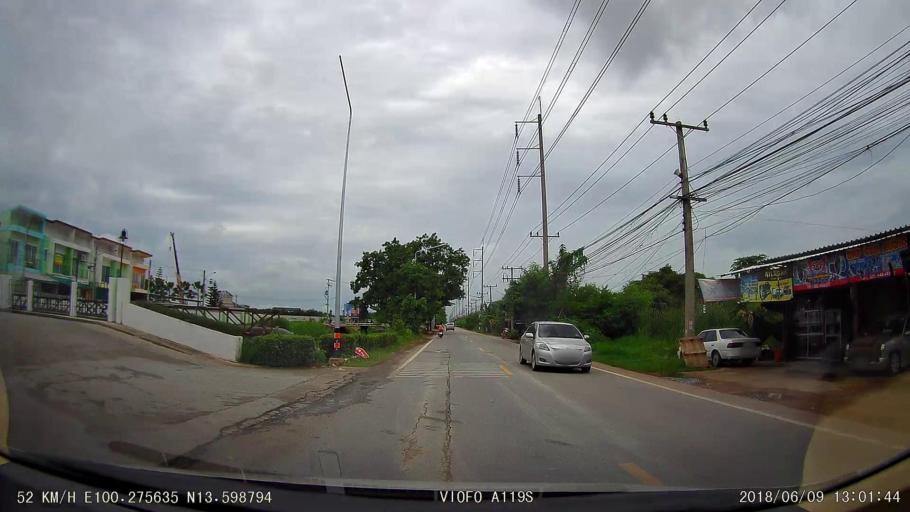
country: TH
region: Samut Sakhon
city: Samut Sakhon
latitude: 13.5988
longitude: 100.2756
